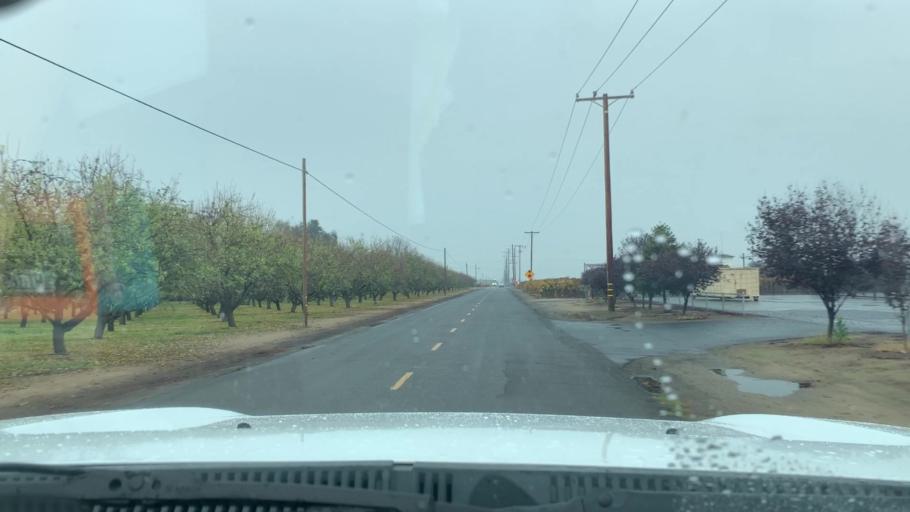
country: US
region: California
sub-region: Tulare County
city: Earlimart
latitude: 35.8339
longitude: -119.2535
